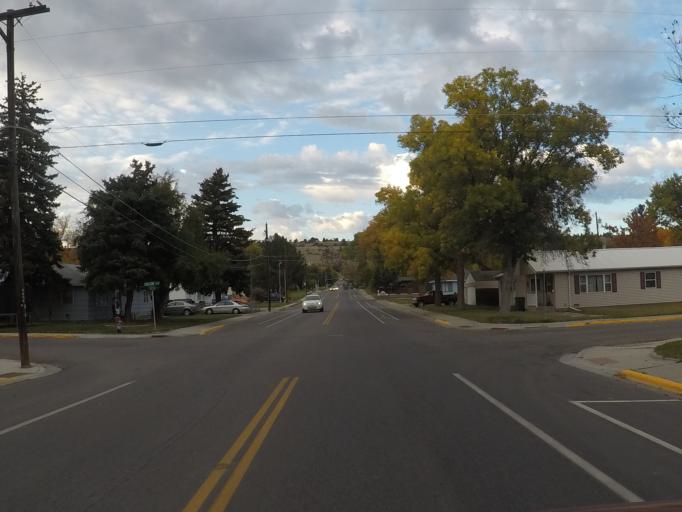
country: US
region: Montana
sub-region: Yellowstone County
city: Billings
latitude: 45.7911
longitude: -108.5486
